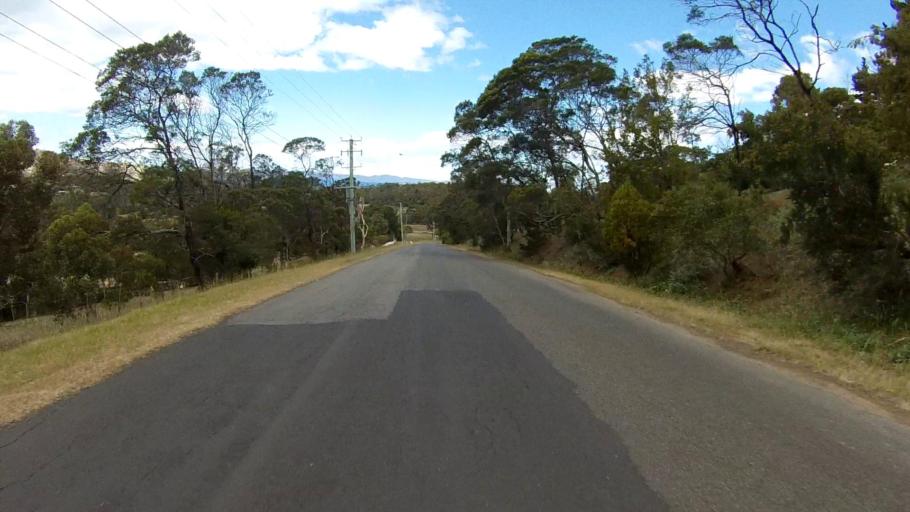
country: AU
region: Tasmania
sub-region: Clarence
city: Acton Park
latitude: -42.8693
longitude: 147.4712
